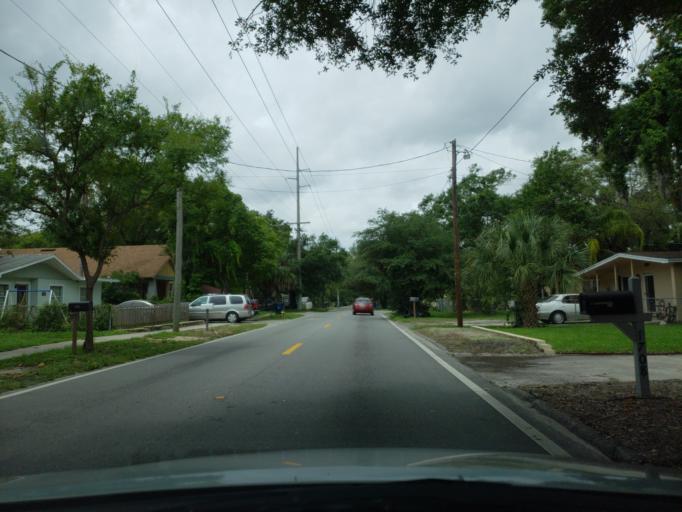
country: US
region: Florida
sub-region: Hillsborough County
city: Tampa
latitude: 28.0034
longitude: -82.4403
